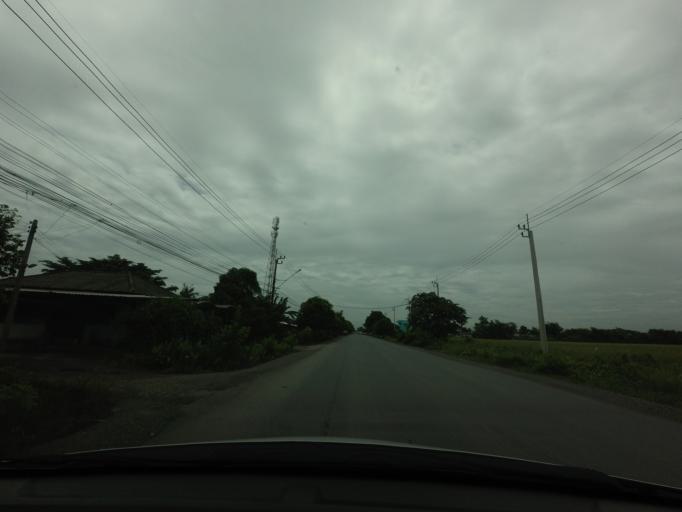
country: TH
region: Bangkok
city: Nong Chok
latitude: 13.8682
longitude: 100.8082
